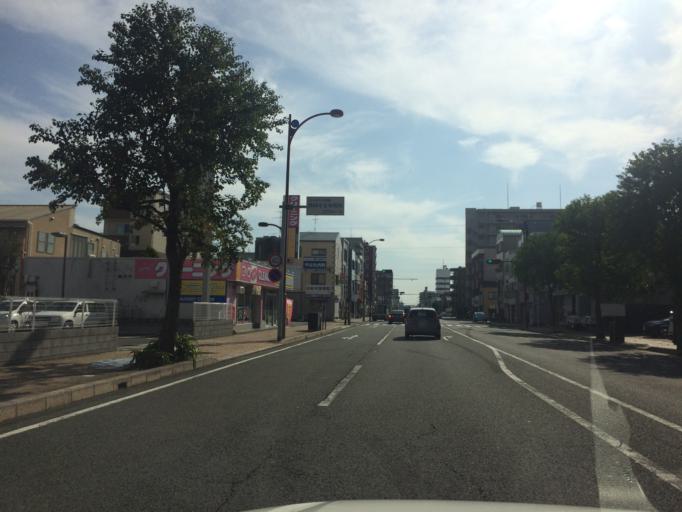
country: JP
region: Shizuoka
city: Shizuoka-shi
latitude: 34.9653
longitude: 138.3952
